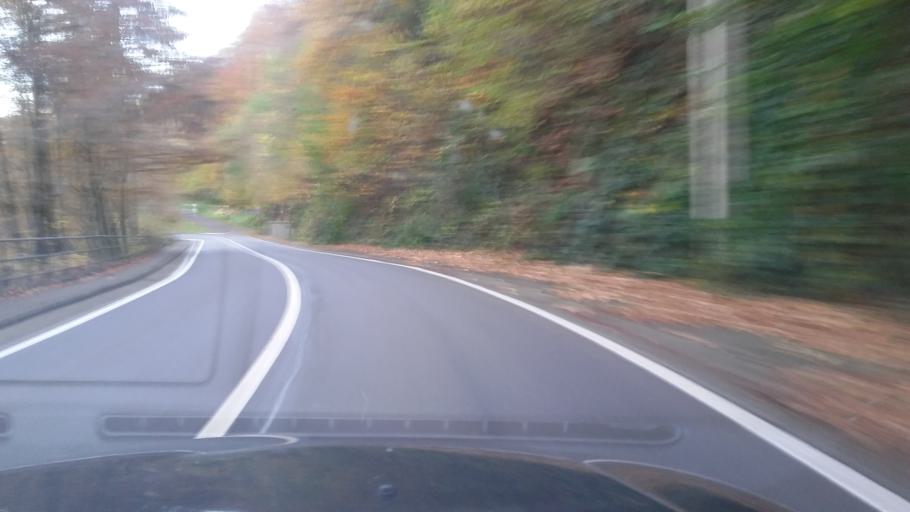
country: BE
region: Wallonia
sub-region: Province du Luxembourg
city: Bouillon
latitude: 49.7849
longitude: 5.0661
